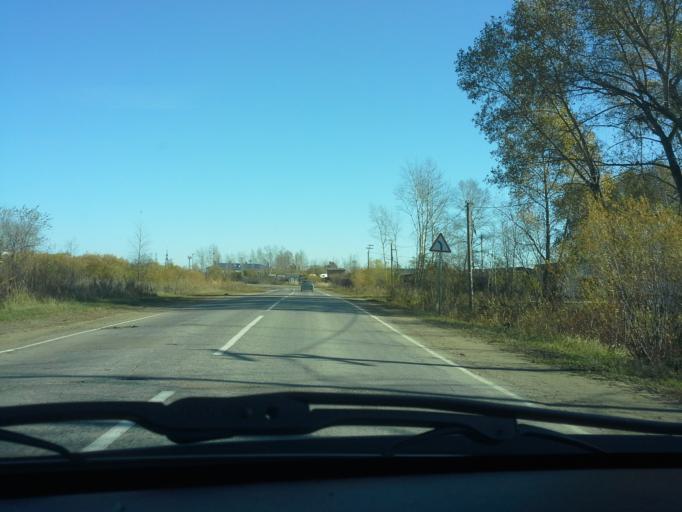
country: RU
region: Jewish Autonomous Oblast
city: Priamurskiy
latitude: 48.5364
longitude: 134.9043
